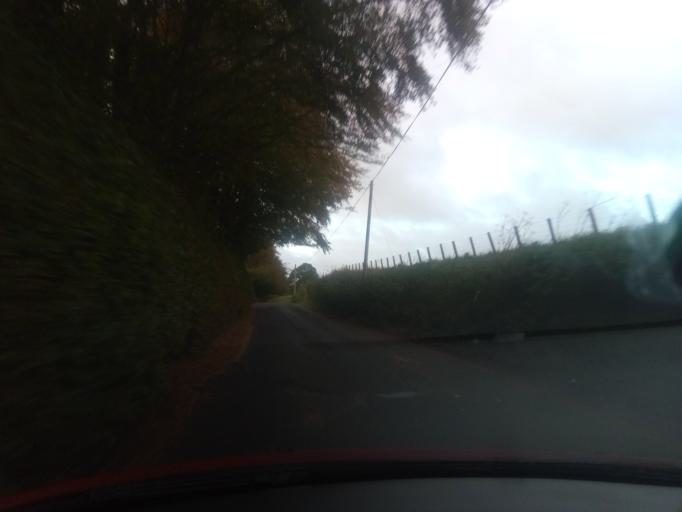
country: GB
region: Scotland
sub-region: The Scottish Borders
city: Jedburgh
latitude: 55.4533
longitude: -2.5648
